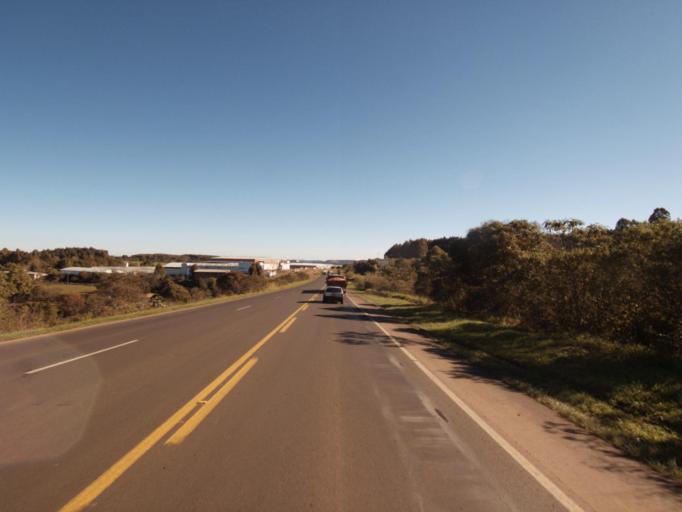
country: BR
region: Santa Catarina
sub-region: Chapeco
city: Chapeco
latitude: -26.9641
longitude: -52.5509
